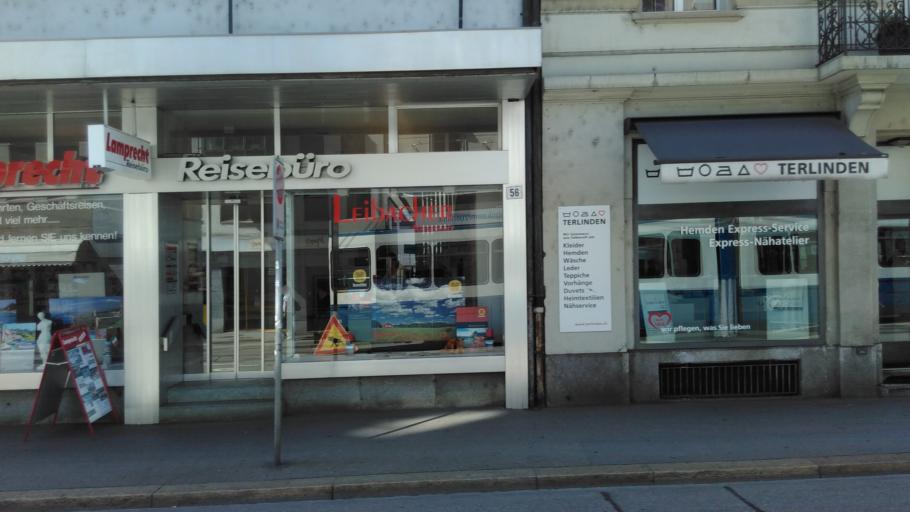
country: CH
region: Zurich
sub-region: Bezirk Zuerich
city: Zuerich (Kreis 1) / City
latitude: 47.3676
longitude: 8.5341
